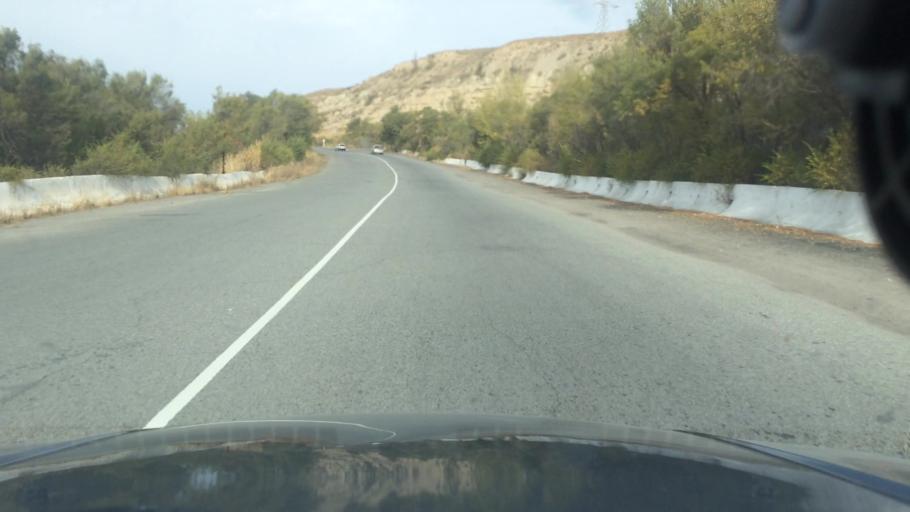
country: KG
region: Ysyk-Koel
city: Karakol
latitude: 42.5945
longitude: 78.3848
